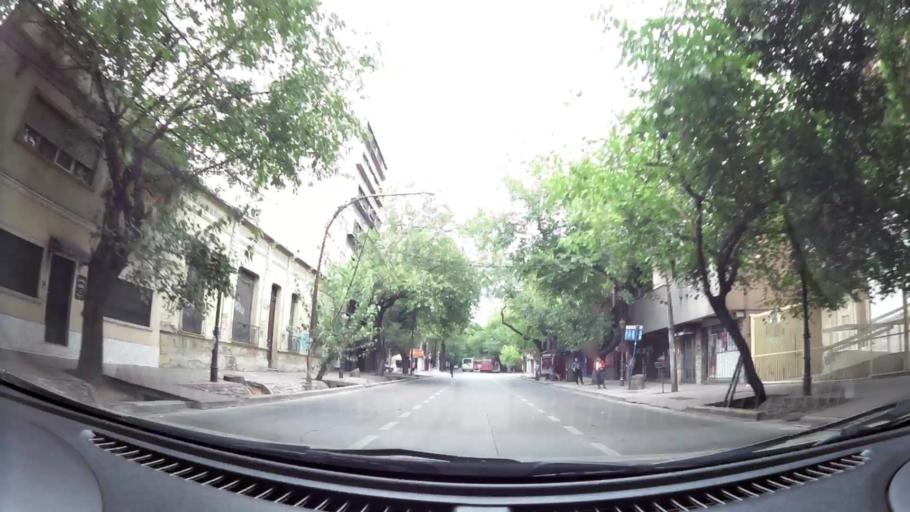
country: AR
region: Mendoza
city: Mendoza
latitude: -32.8939
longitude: -68.8443
